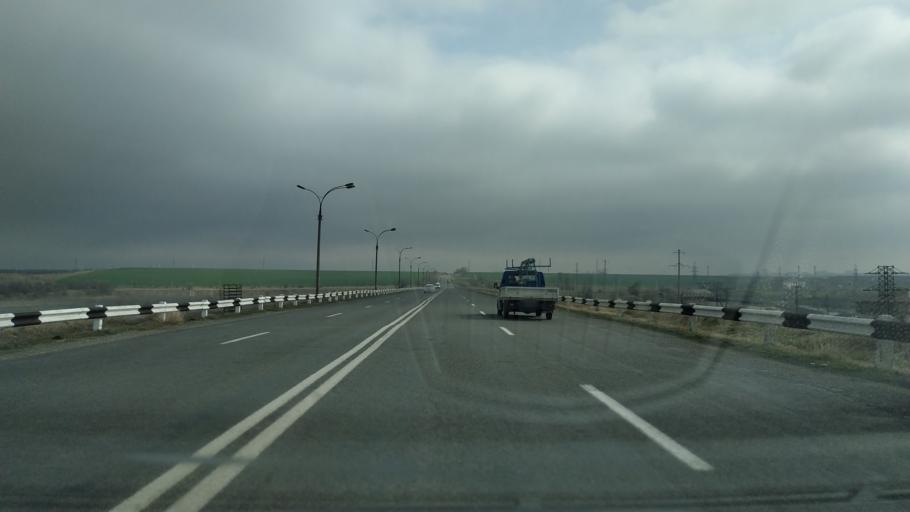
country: MD
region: Straseni
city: Taraclia
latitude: 45.9371
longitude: 28.6123
